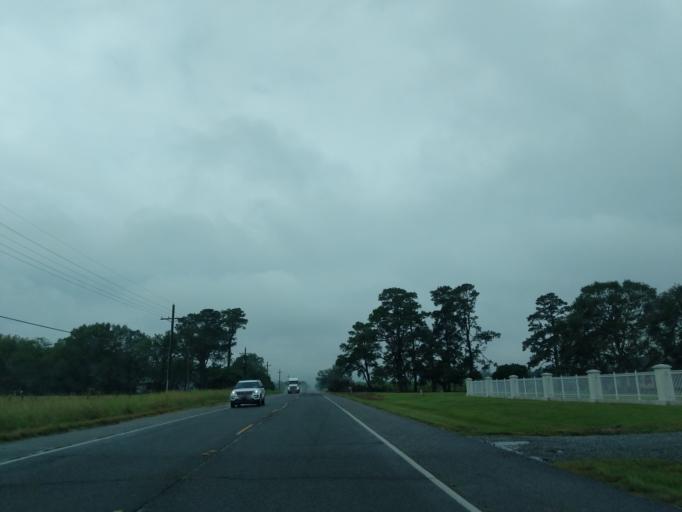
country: US
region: Louisiana
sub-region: Vermilion Parish
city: Kaplan
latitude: 29.9915
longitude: -92.2152
